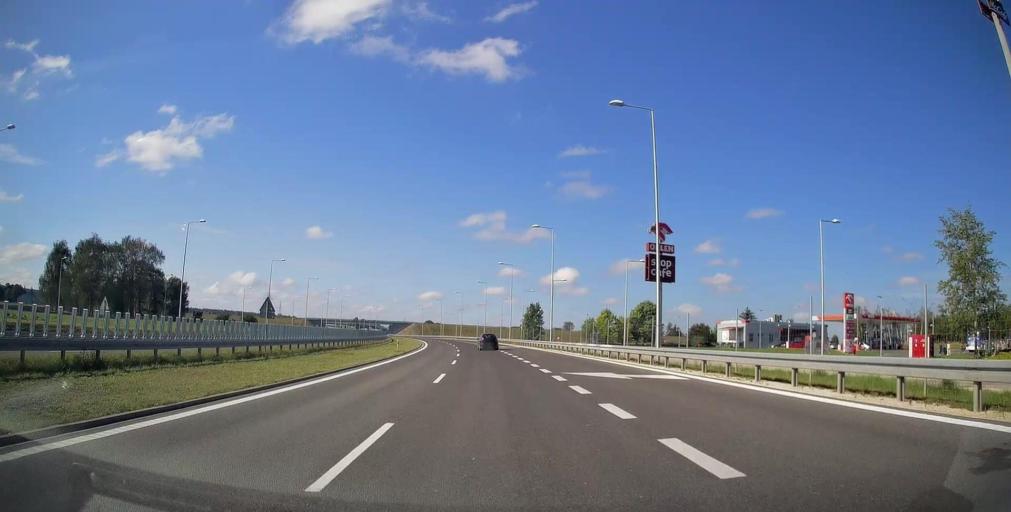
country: PL
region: Swietokrzyskie
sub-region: Powiat jedrzejowski
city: Jedrzejow
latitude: 50.6231
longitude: 20.2851
